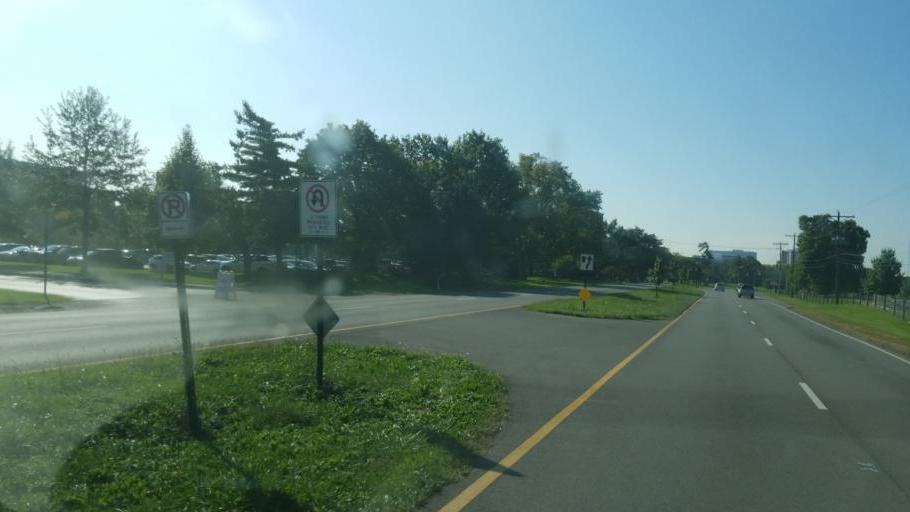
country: US
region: Ohio
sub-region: Franklin County
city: Grandview Heights
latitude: 40.0142
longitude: -83.0224
